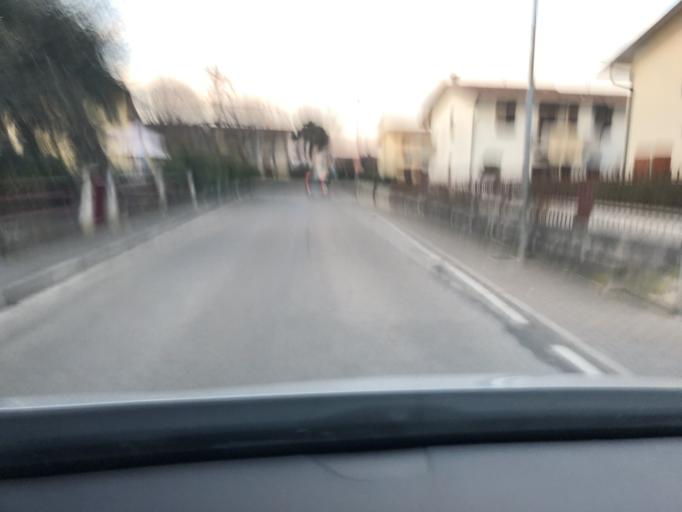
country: IT
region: Veneto
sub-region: Provincia di Verona
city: Sommacampagna
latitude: 45.4054
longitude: 10.8496
